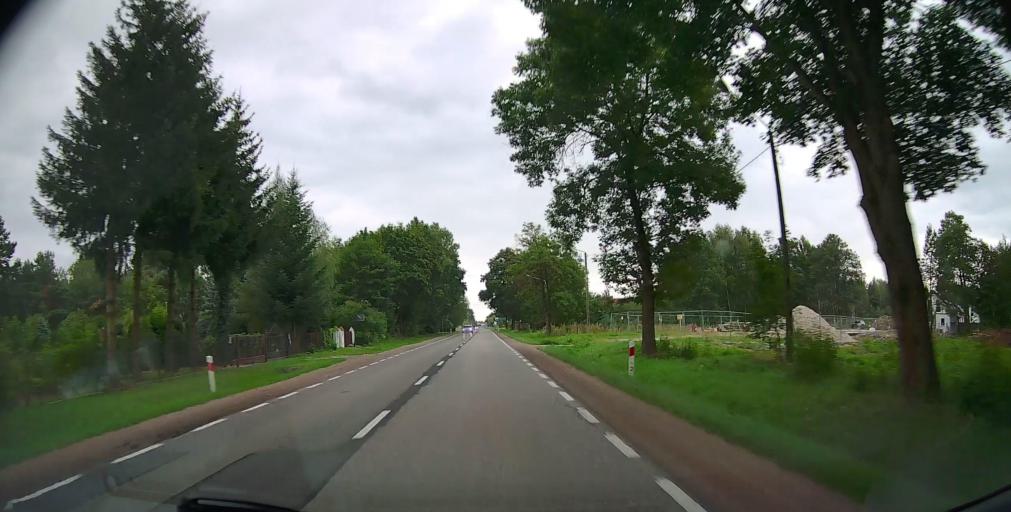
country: PL
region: Masovian Voivodeship
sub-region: Powiat radomski
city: Zakrzew
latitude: 51.4268
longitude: 21.0550
